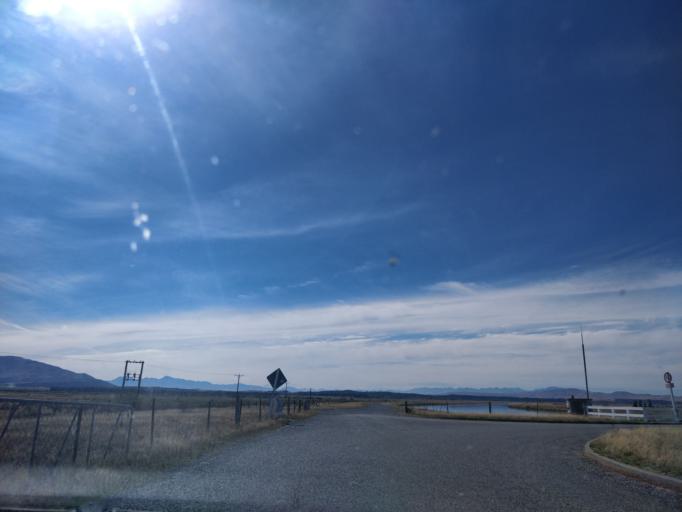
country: NZ
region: Otago
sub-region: Queenstown-Lakes District
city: Wanaka
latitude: -44.2202
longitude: 170.0498
